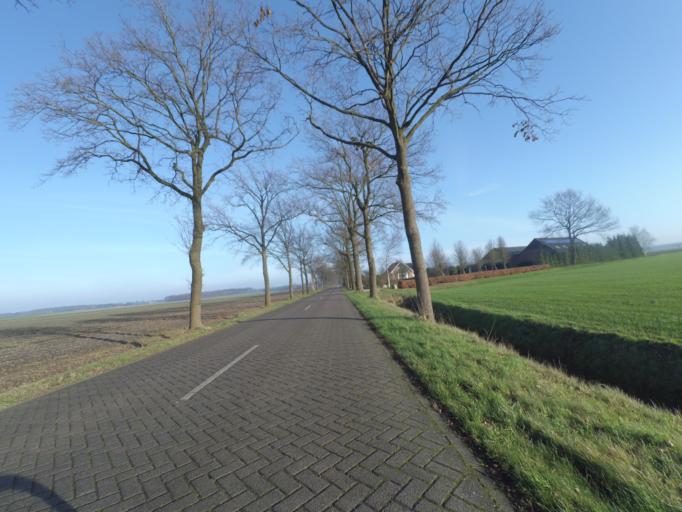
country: NL
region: Drenthe
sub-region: Gemeente Borger-Odoorn
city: Borger
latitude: 52.8687
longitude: 6.7697
